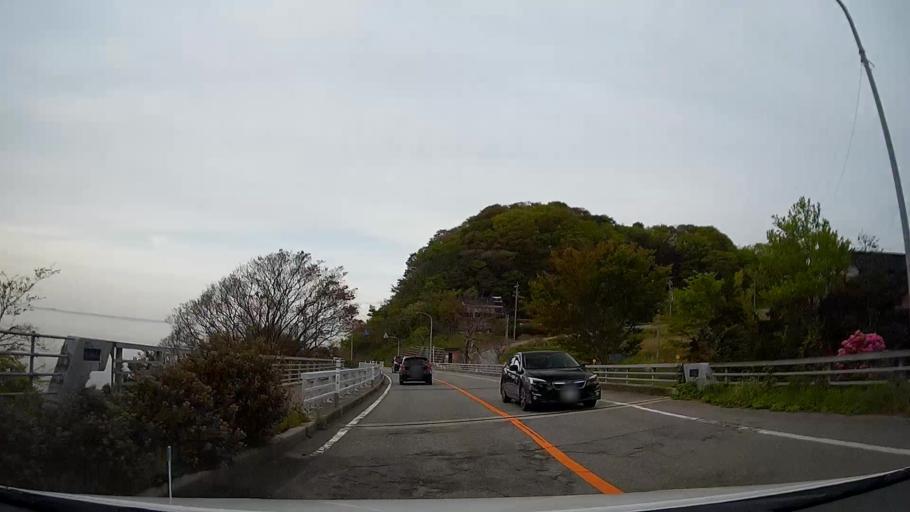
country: JP
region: Ishikawa
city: Nanao
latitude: 37.4075
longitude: 136.9604
